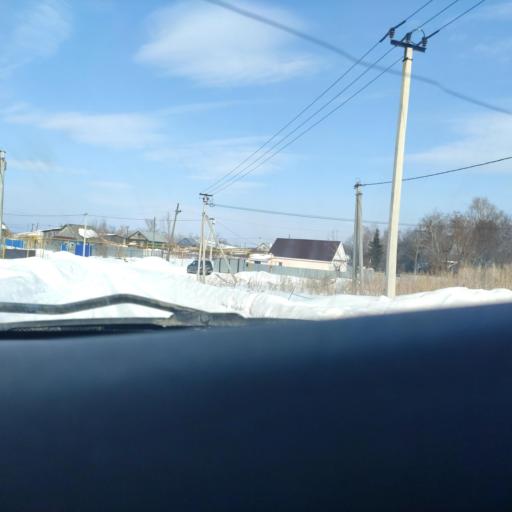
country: RU
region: Samara
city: Rozhdestveno
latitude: 53.2449
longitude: 50.0631
